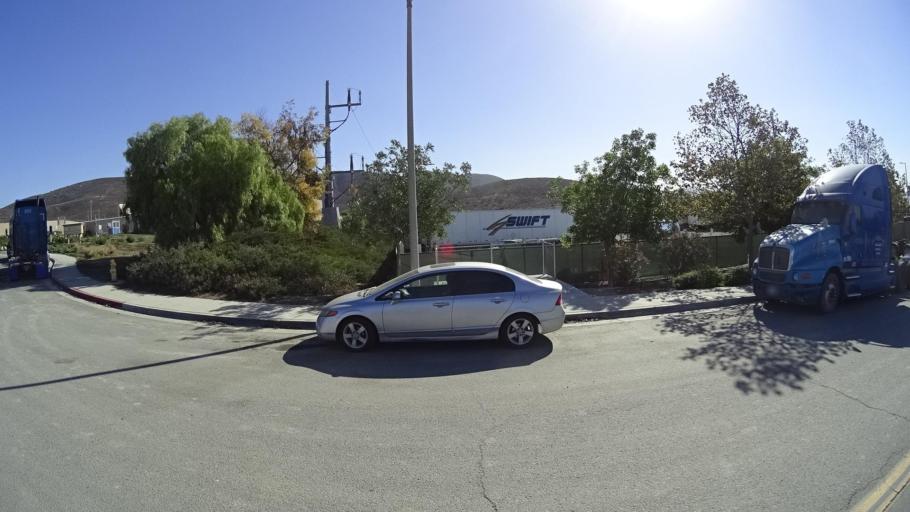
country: MX
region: Baja California
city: Tijuana
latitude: 32.5718
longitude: -116.9168
